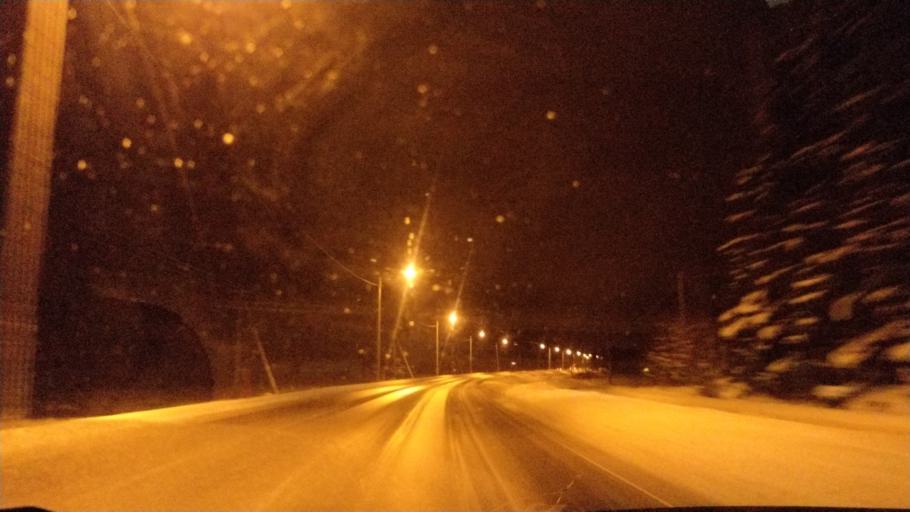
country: FI
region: Lapland
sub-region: Rovaniemi
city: Rovaniemi
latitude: 66.3110
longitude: 25.3617
